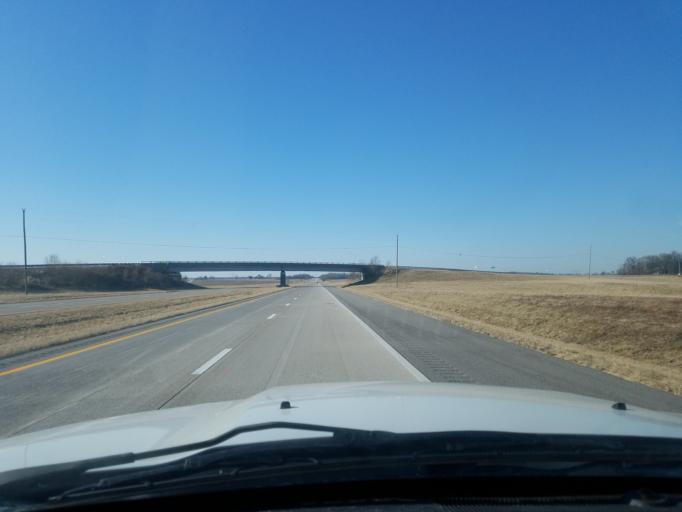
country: US
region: Kentucky
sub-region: Henderson County
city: Henderson
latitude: 37.7854
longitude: -87.4697
